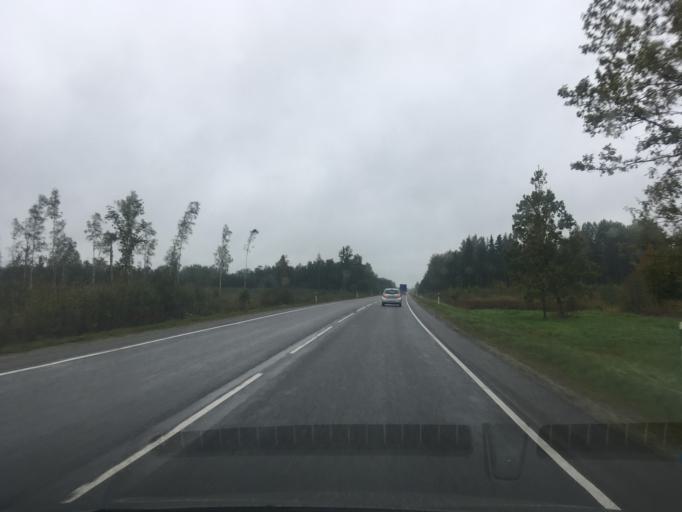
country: EE
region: Jaervamaa
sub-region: Paide linn
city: Paide
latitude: 58.8141
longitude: 25.7575
